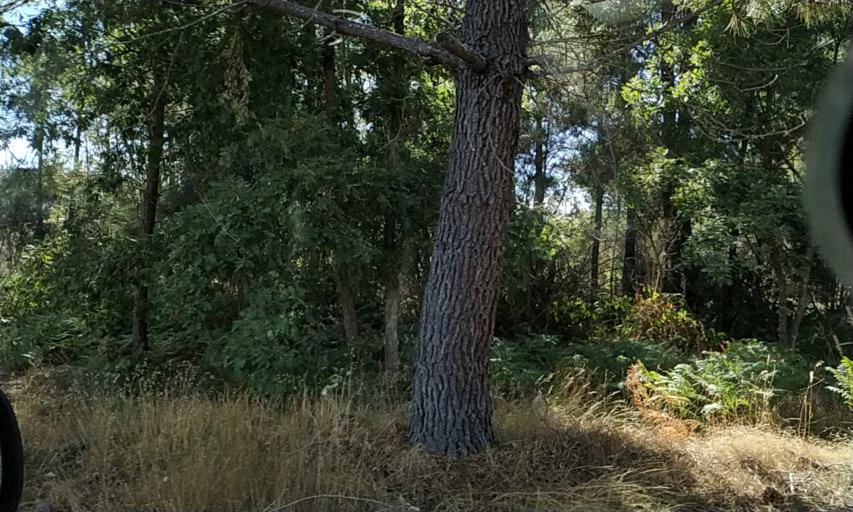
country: PT
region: Vila Real
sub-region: Sabrosa
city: Sabrosa
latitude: 41.3586
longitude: -7.5897
